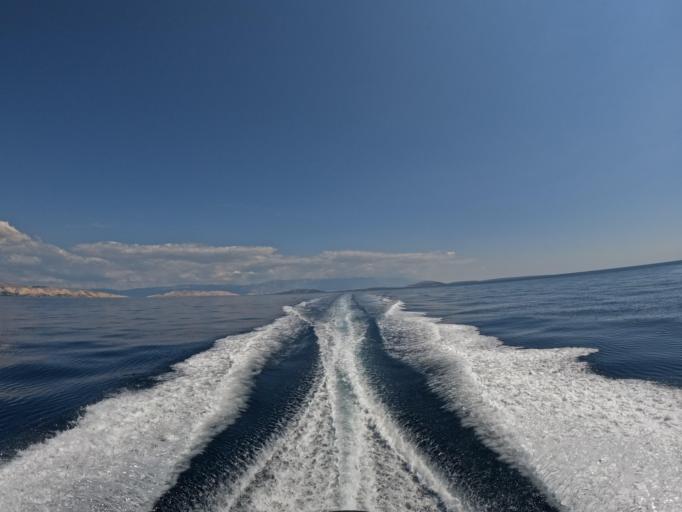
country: HR
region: Primorsko-Goranska
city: Punat
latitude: 44.9140
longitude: 14.5826
